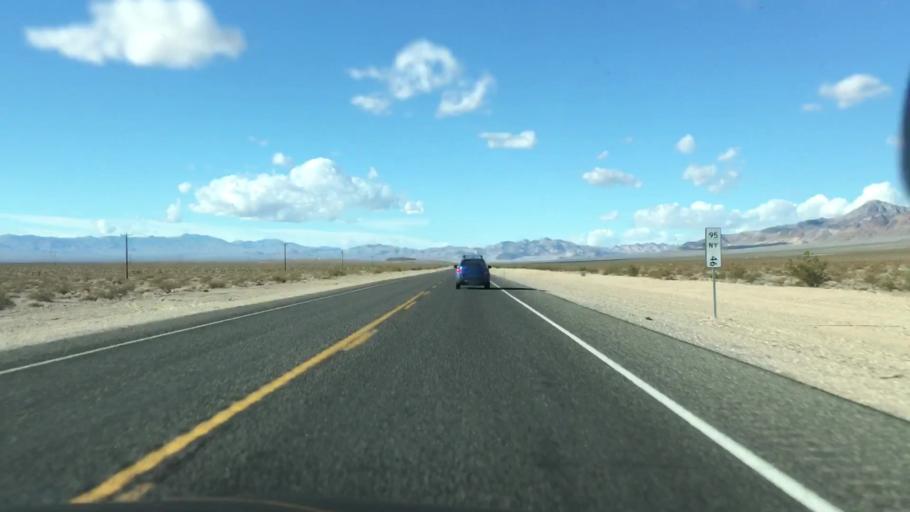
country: US
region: Nevada
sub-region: Nye County
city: Beatty
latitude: 36.7437
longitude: -116.6482
